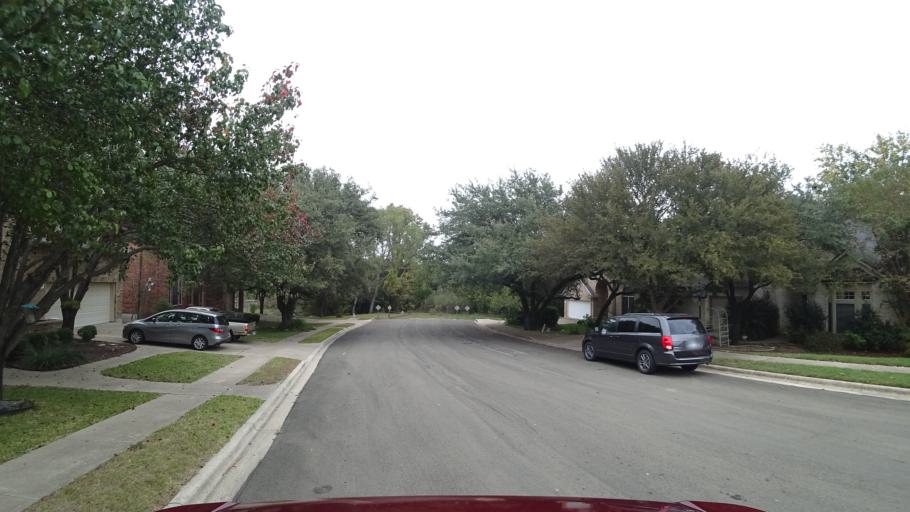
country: US
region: Texas
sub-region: Williamson County
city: Anderson Mill
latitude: 30.4337
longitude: -97.8271
